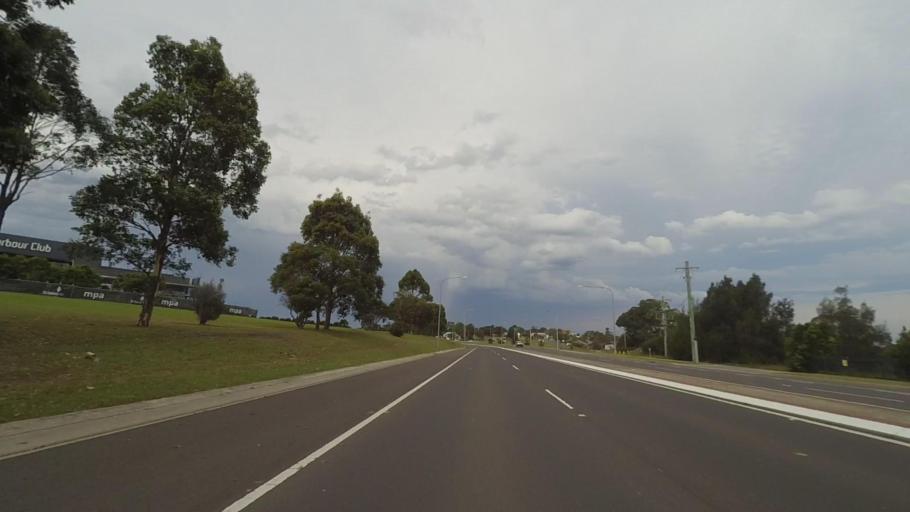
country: AU
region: New South Wales
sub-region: Shellharbour
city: Flinders
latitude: -34.5832
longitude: 150.8586
